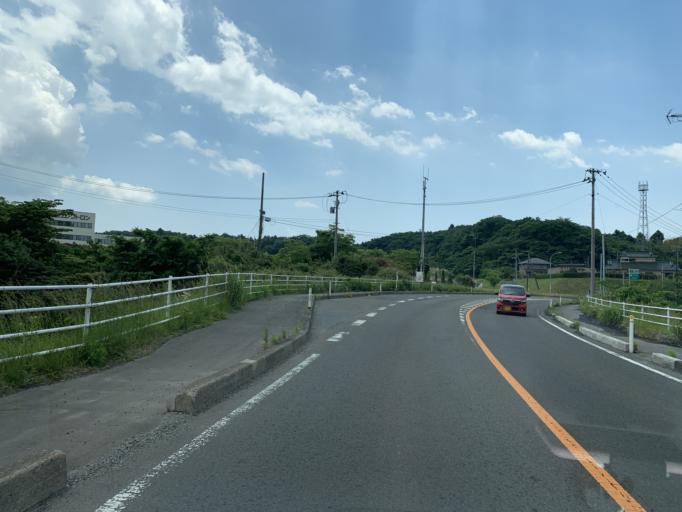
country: JP
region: Miyagi
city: Matsushima
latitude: 38.4067
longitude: 141.0668
